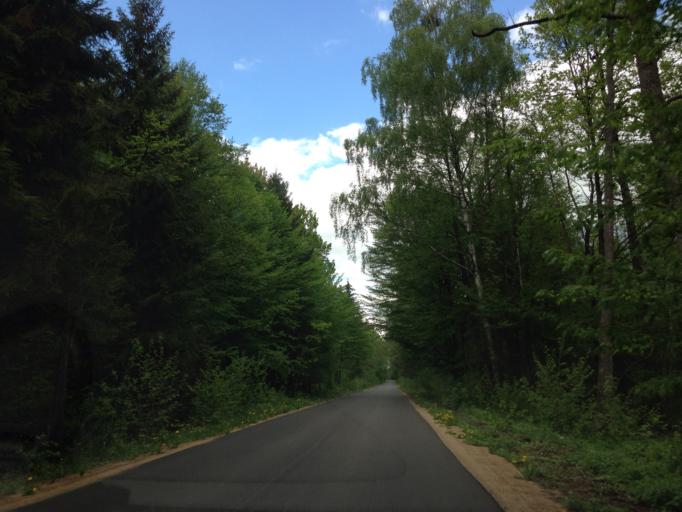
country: PL
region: Podlasie
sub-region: Powiat grajewski
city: Radzilow
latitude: 53.3373
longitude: 22.5988
